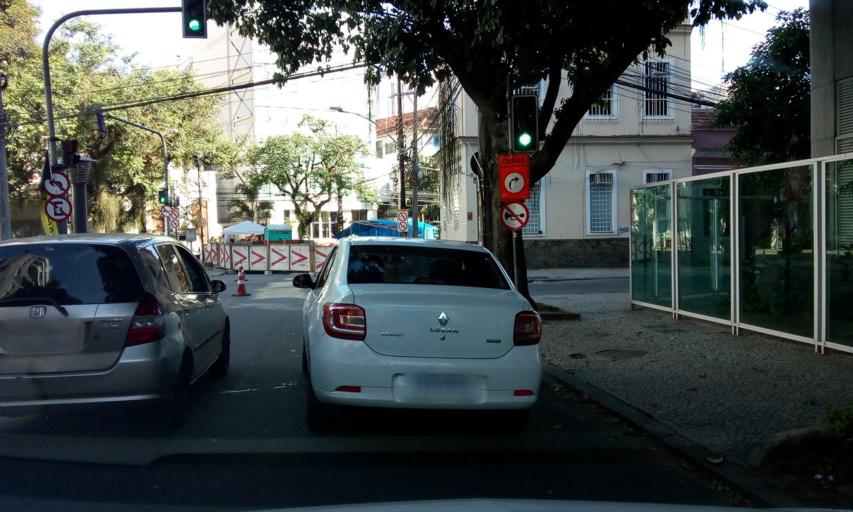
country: BR
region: Rio de Janeiro
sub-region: Rio De Janeiro
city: Rio de Janeiro
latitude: -22.9564
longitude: -43.1849
